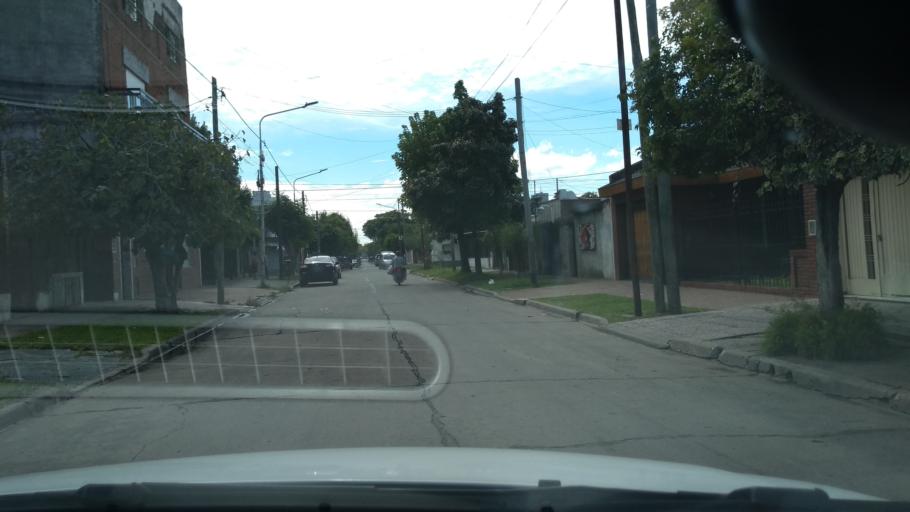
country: AR
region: Buenos Aires
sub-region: Partido de Moron
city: Moron
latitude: -34.6642
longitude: -58.6104
